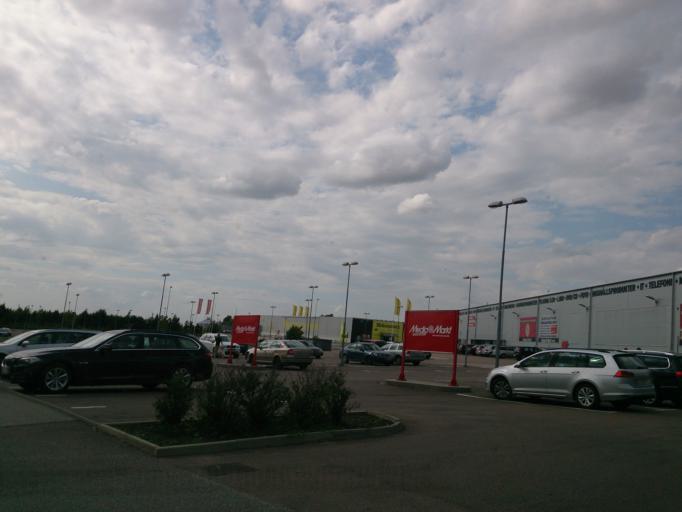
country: SE
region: Skane
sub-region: Lunds Kommun
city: Lund
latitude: 55.7136
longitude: 13.1532
